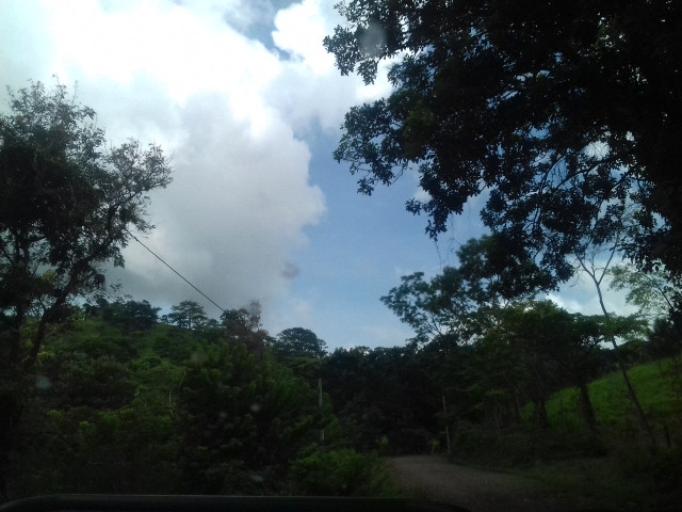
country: NI
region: Matagalpa
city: Matiguas
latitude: 12.9046
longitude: -85.3599
